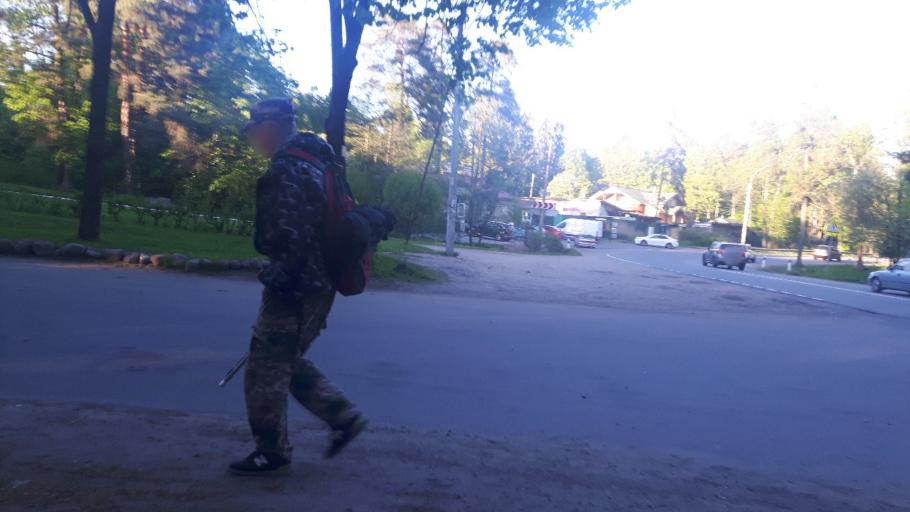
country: RU
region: St.-Petersburg
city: Zelenogorsk
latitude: 60.1939
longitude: 29.6667
